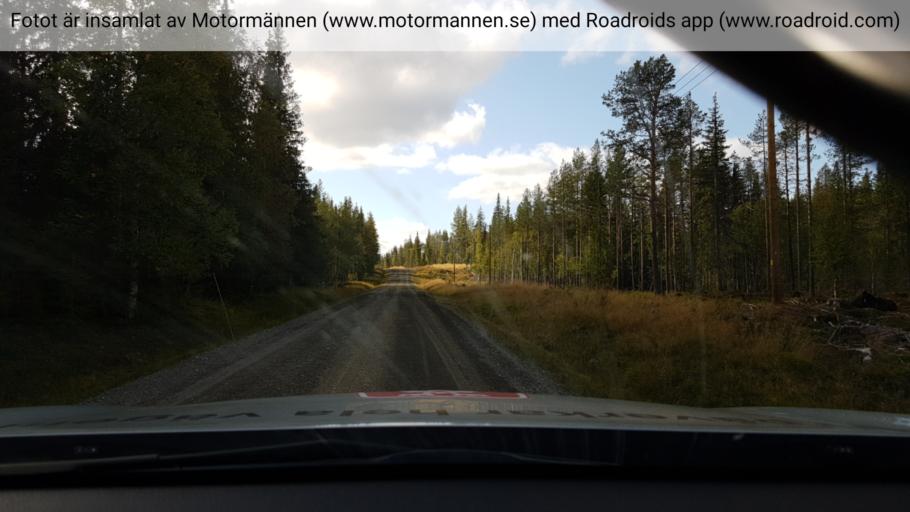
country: SE
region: Vaesterbotten
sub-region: Mala Kommun
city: Mala
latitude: 65.4919
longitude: 18.2605
